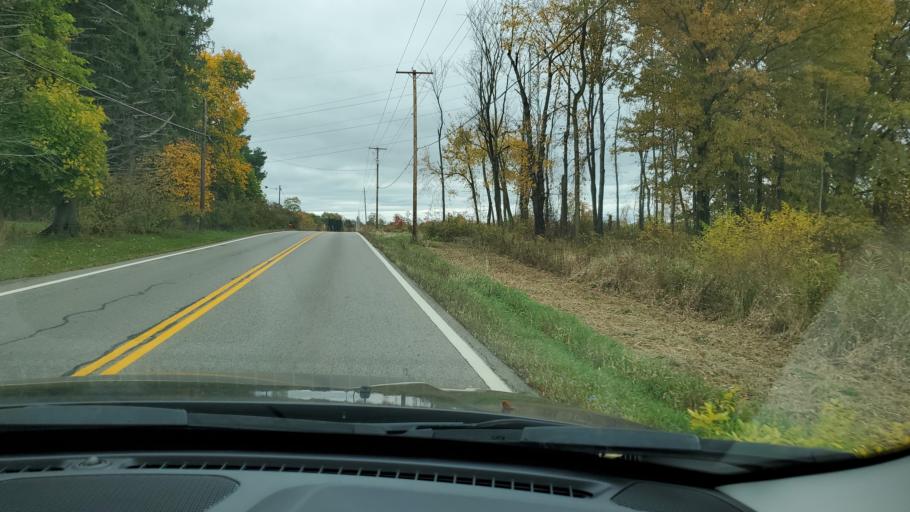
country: US
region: Ohio
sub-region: Mahoning County
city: New Middletown
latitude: 40.9379
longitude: -80.6314
